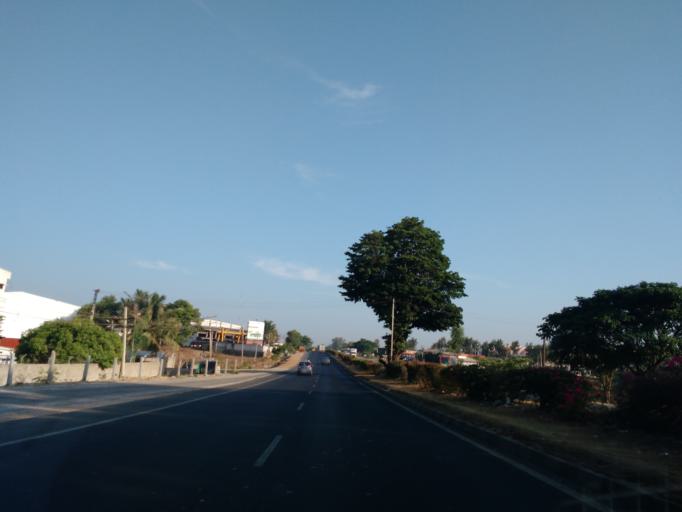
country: IN
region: Karnataka
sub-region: Bangalore Rural
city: Nelamangala
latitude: 13.1342
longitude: 77.3561
